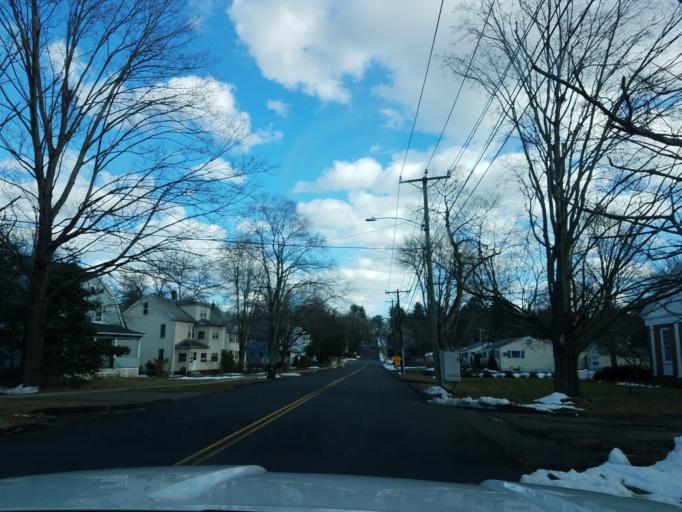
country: US
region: Connecticut
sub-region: Hartford County
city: Kensington
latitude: 41.6243
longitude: -72.7497
